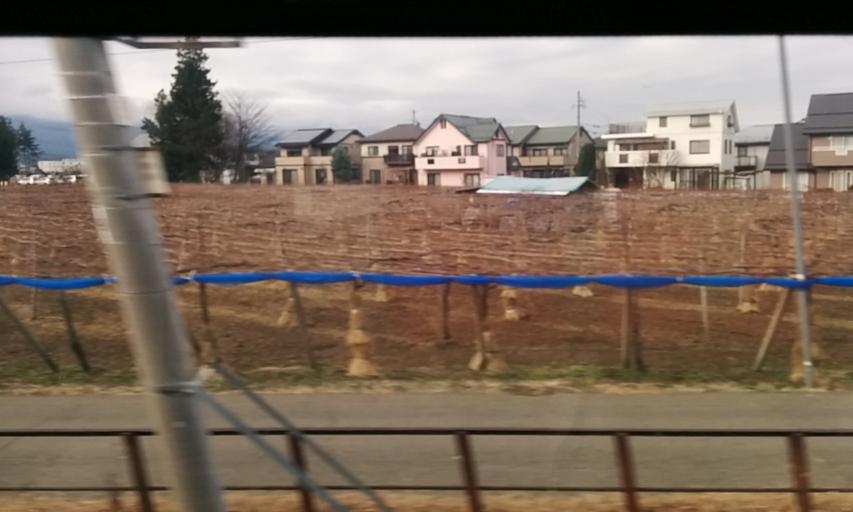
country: JP
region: Nagano
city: Shiojiri
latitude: 36.1080
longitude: 137.9417
